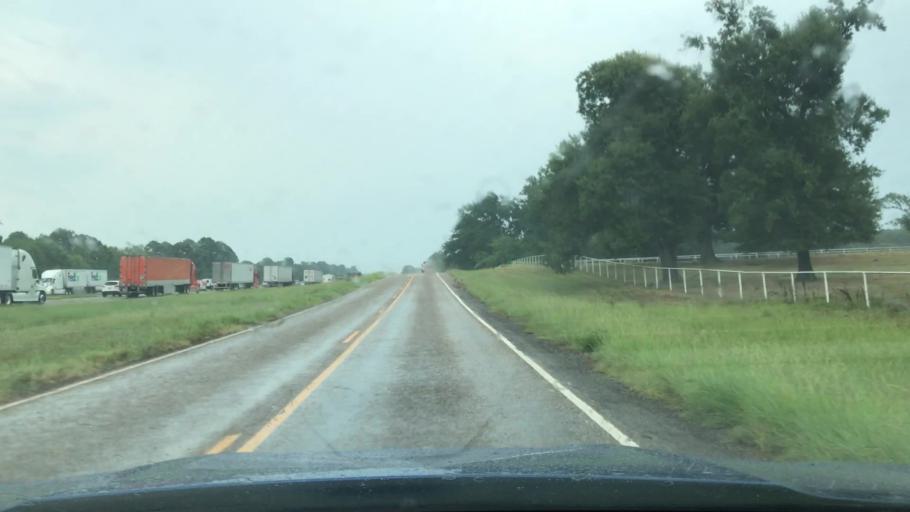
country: US
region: Texas
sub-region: Harrison County
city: Waskom
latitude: 32.4867
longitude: -94.1305
